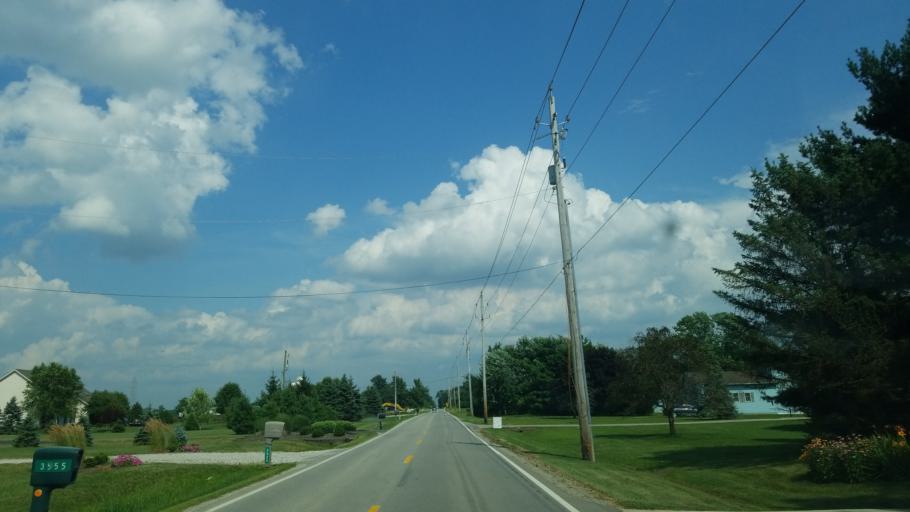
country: US
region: Ohio
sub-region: Delaware County
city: Powell
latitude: 40.2168
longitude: -83.1049
